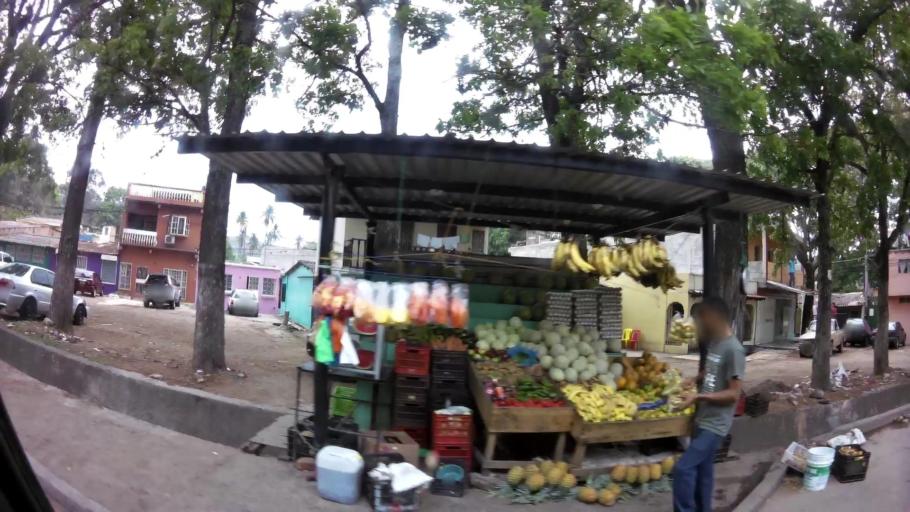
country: HN
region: Francisco Morazan
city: Tegucigalpa
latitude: 14.0634
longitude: -87.2009
